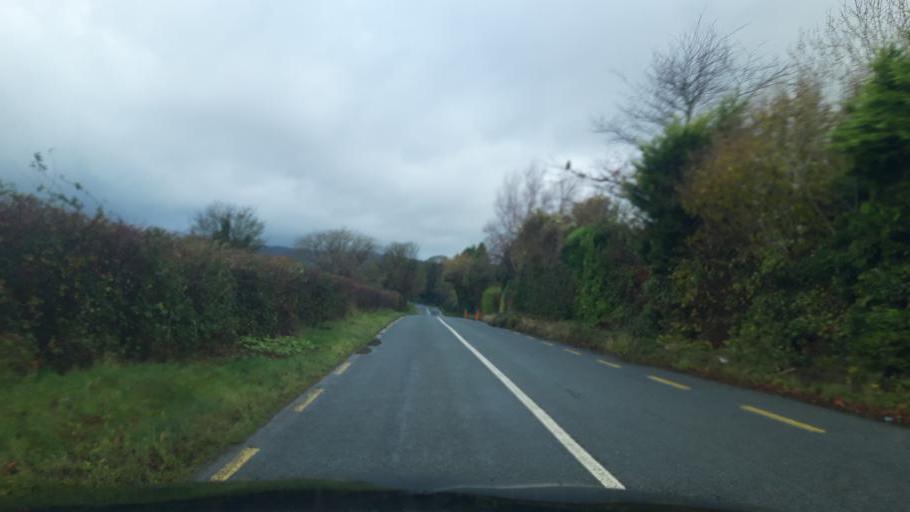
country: IE
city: Kilquade
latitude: 53.0968
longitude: -6.0887
